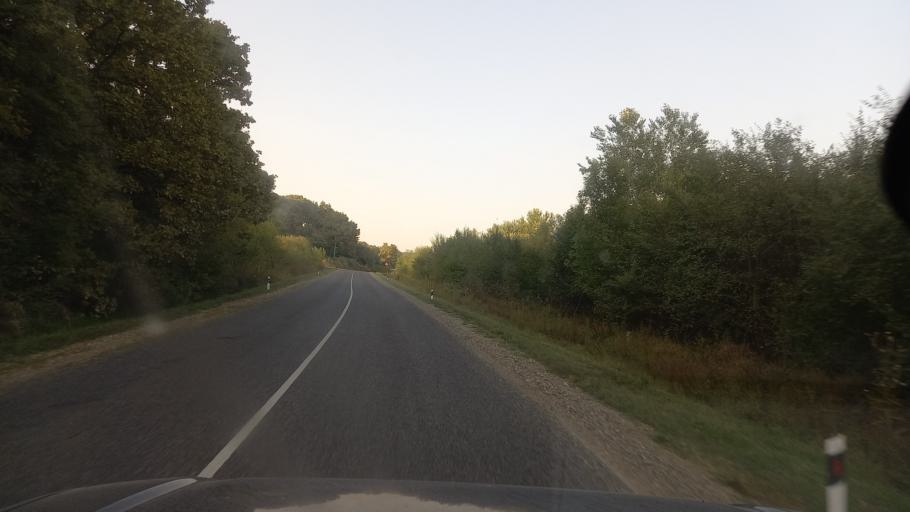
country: RU
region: Krasnodarskiy
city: Smolenskaya
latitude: 44.7507
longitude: 38.7624
